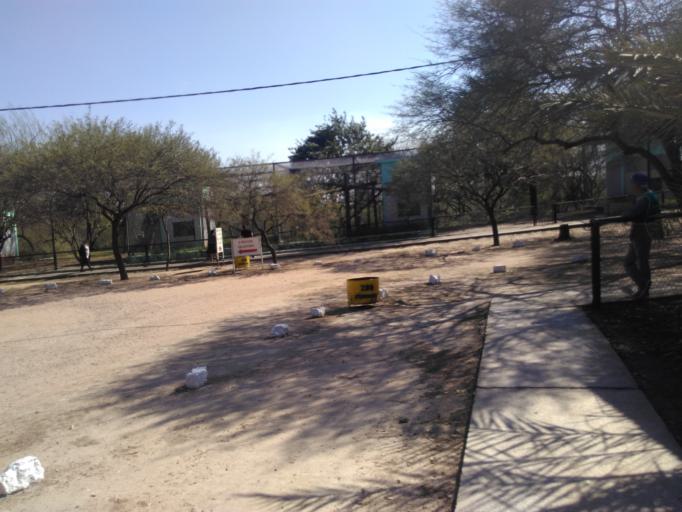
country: AR
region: Chaco
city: Presidencia Roque Saenz Pena
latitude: -26.8186
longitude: -60.4185
